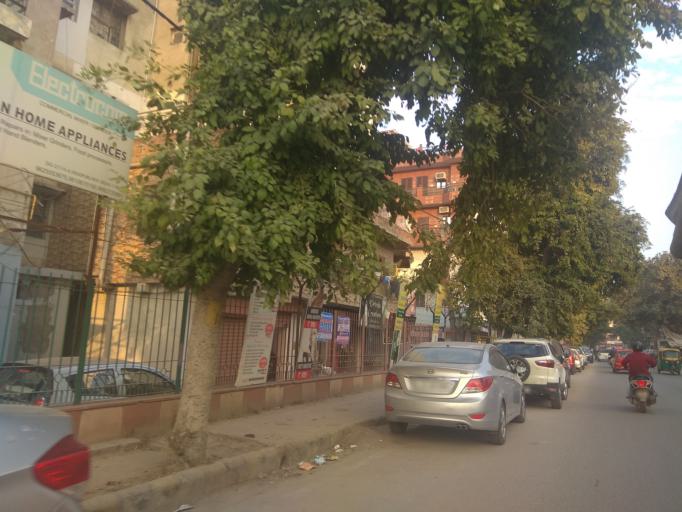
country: IN
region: NCT
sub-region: West Delhi
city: Nangloi Jat
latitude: 28.6345
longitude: 77.0663
